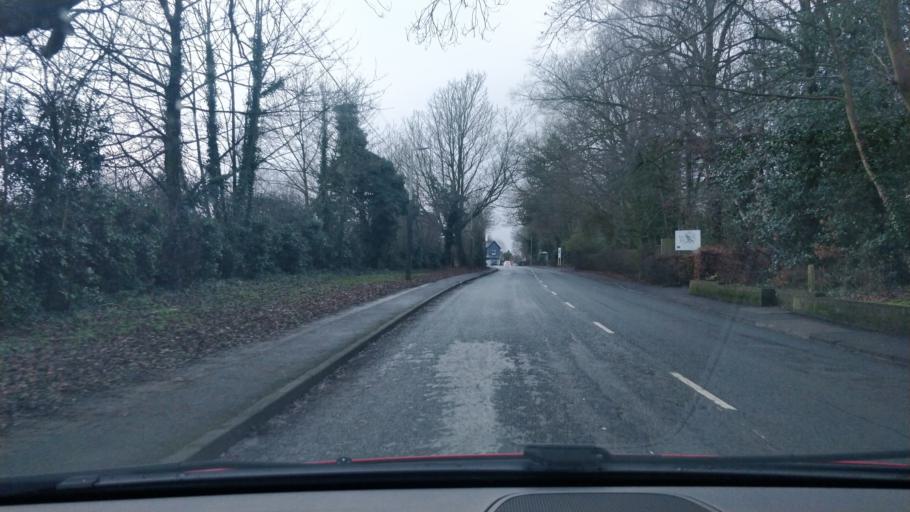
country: GB
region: England
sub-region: Lancashire
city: Croston
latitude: 53.7287
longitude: -2.7794
